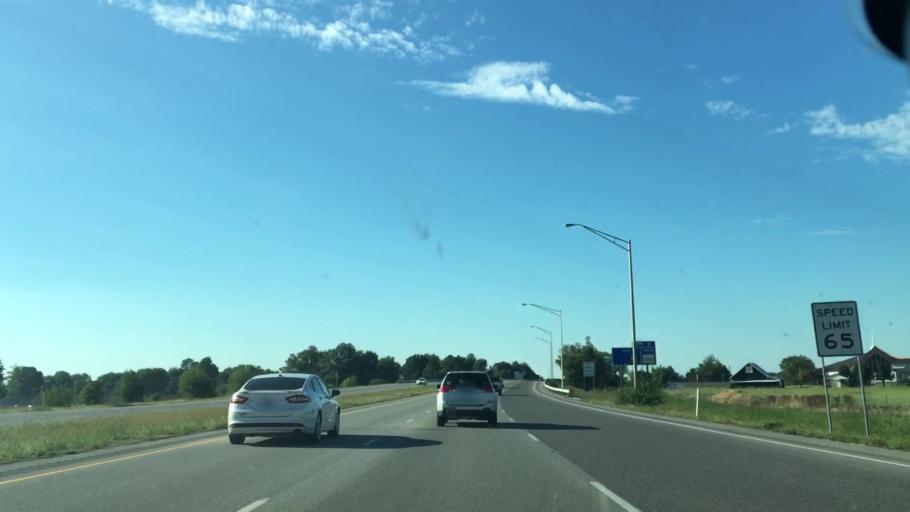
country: US
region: Kentucky
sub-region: Daviess County
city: Owensboro
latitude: 37.7468
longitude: -87.1539
